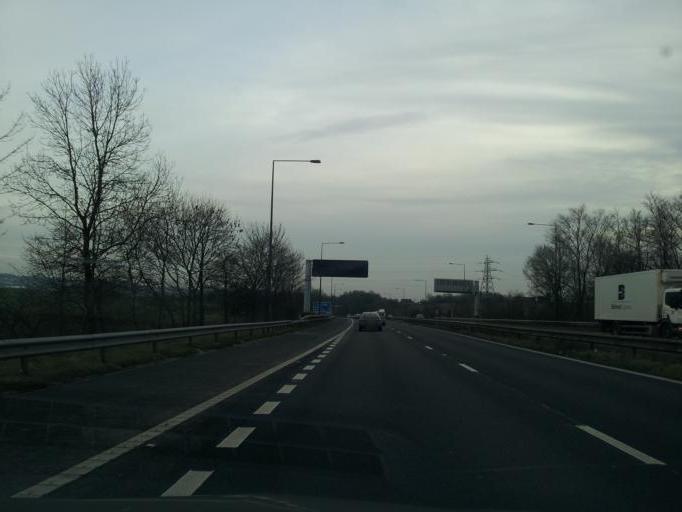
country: GB
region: England
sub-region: Borough of Oldham
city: Royton
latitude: 53.5687
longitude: -2.1574
